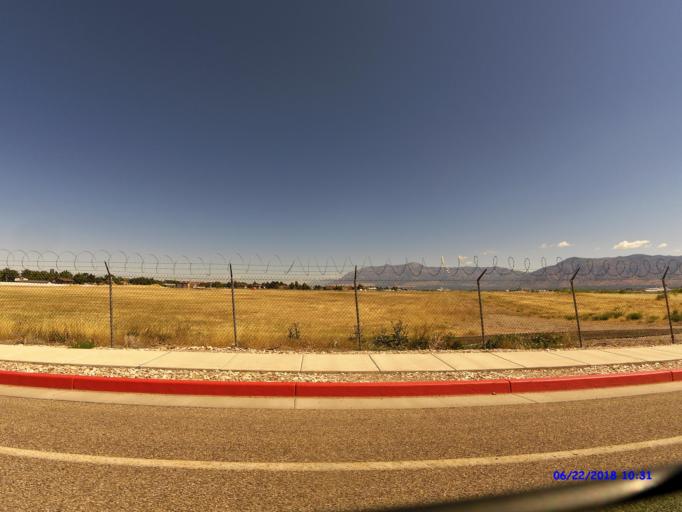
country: US
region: Utah
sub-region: Weber County
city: Riverdale
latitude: 41.1835
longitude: -112.0241
